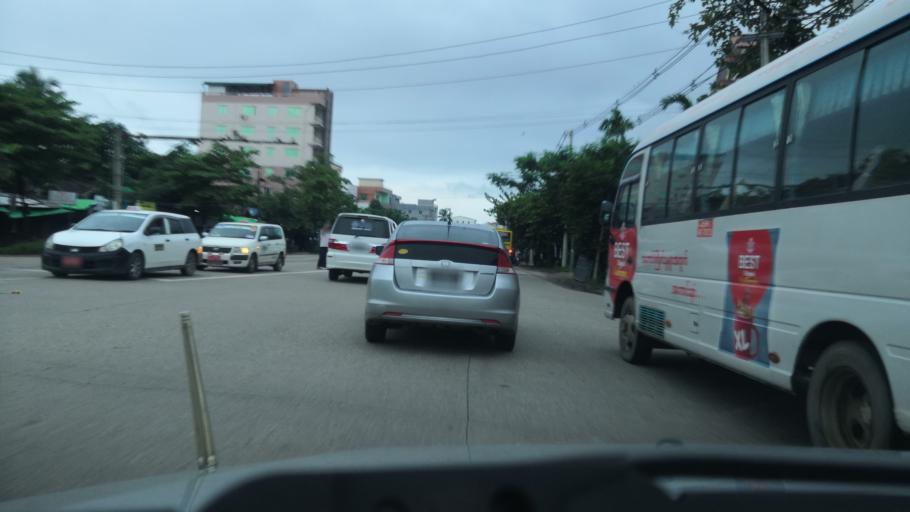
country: MM
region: Yangon
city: Yangon
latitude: 16.8613
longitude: 96.1773
